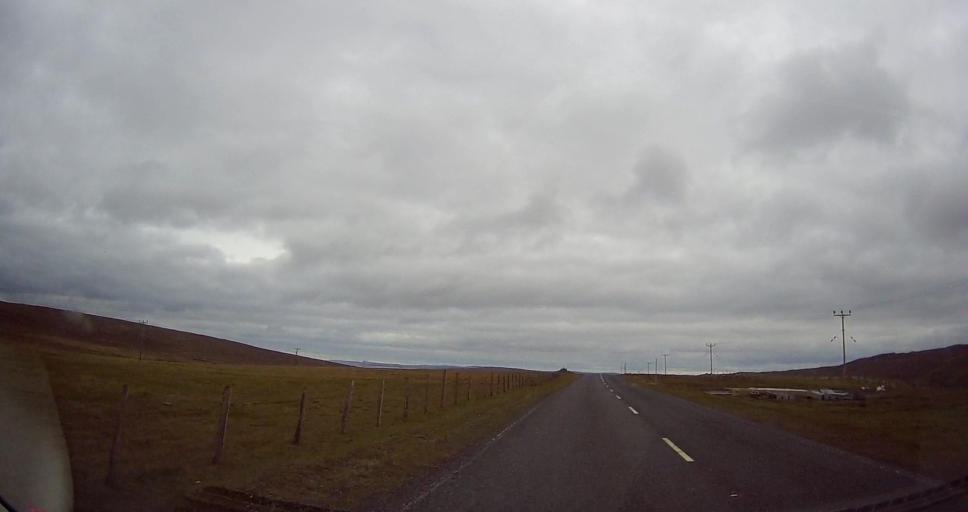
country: GB
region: Scotland
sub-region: Shetland Islands
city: Shetland
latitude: 60.7300
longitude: -0.8975
